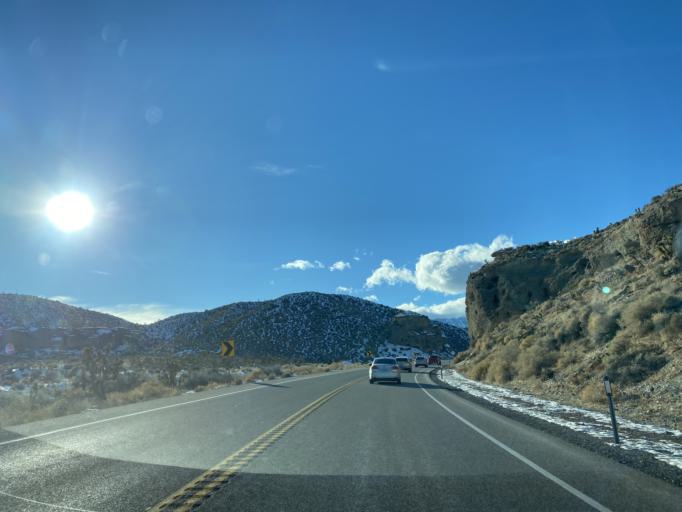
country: US
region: Nevada
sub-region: Clark County
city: Summerlin South
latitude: 36.2763
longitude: -115.4954
